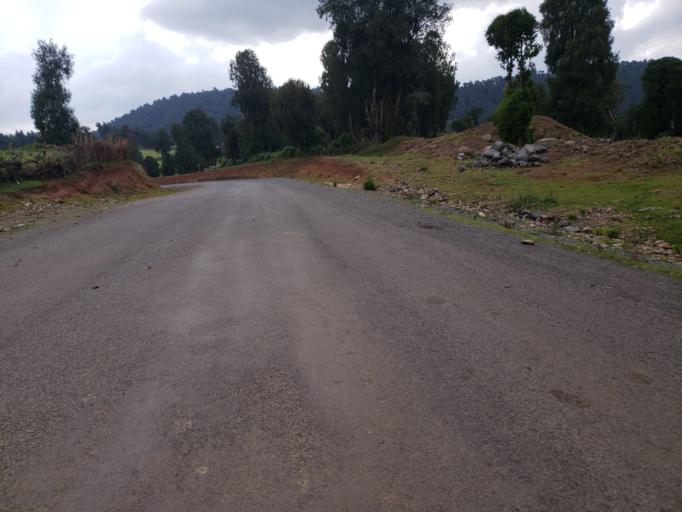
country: ET
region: Oromiya
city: Dodola
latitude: 6.8874
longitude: 39.3889
